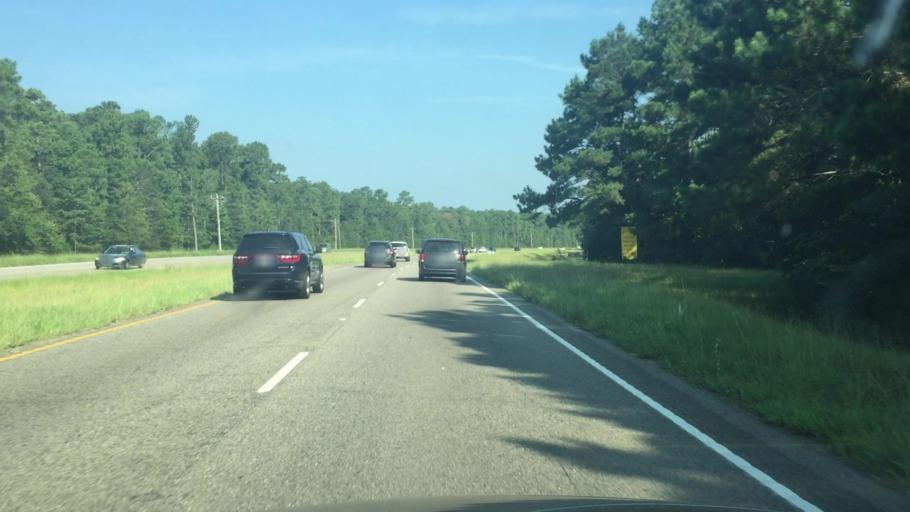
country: US
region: South Carolina
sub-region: Horry County
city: North Myrtle Beach
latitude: 33.9157
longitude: -78.7200
